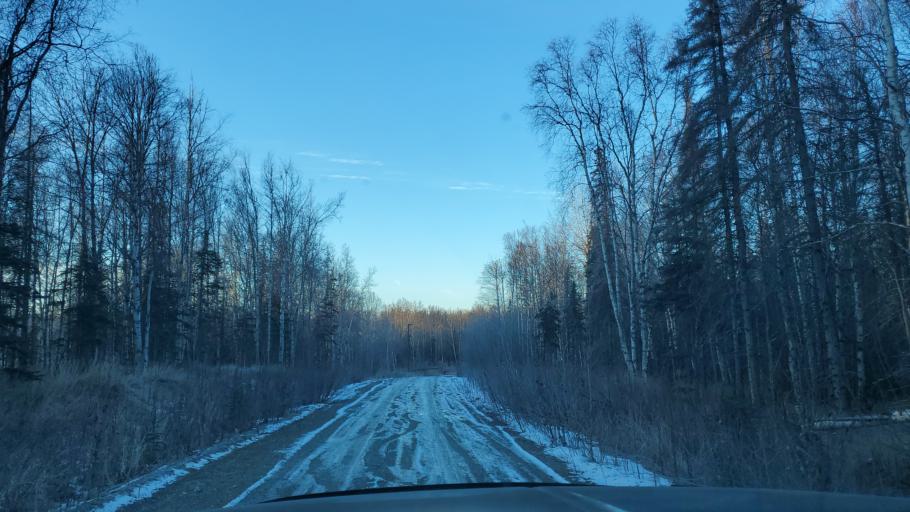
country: US
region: Alaska
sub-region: Matanuska-Susitna Borough
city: Lakes
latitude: 61.6537
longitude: -149.3337
